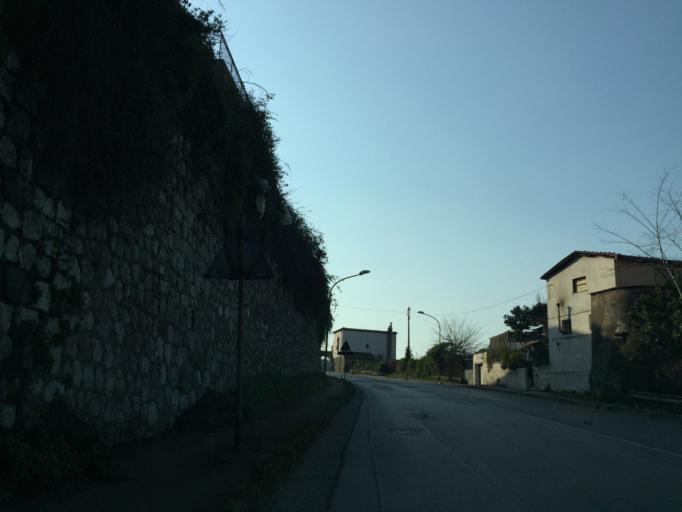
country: IT
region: Campania
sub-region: Provincia di Napoli
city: Castellammare di Stabia
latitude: 40.6886
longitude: 14.4885
